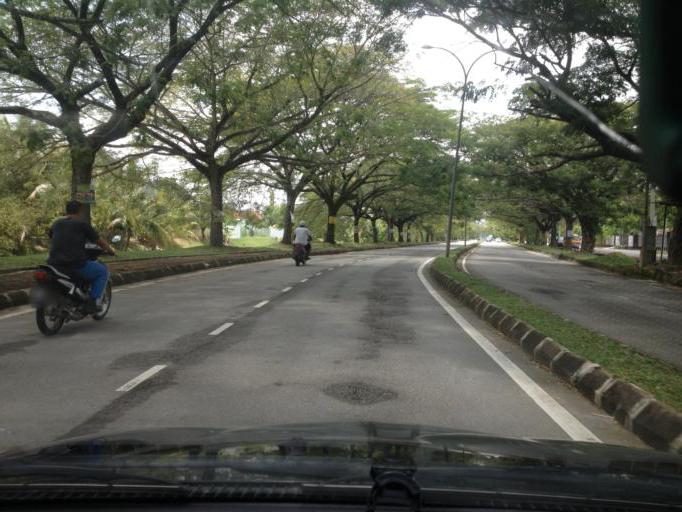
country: MY
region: Kedah
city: Sungai Petani
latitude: 5.6051
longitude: 100.5417
